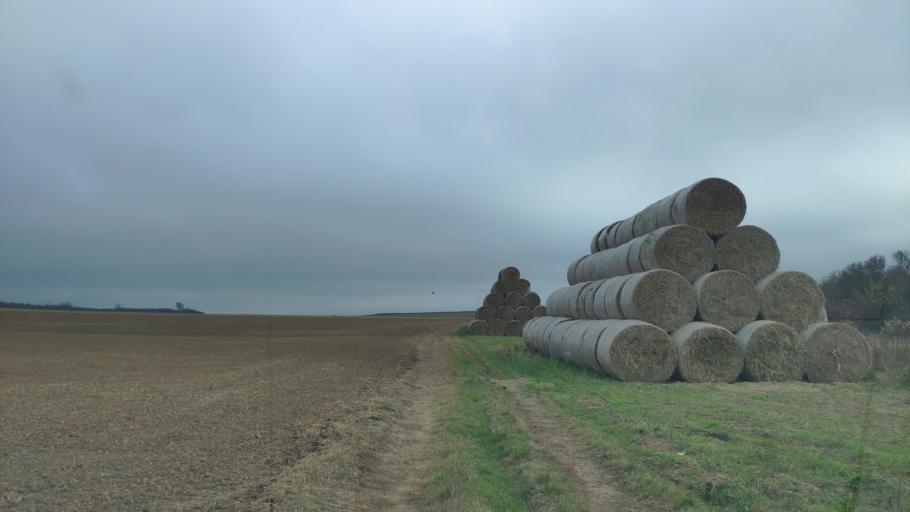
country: SK
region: Presovsky
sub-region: Okres Presov
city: Presov
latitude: 49.0170
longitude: 21.2043
